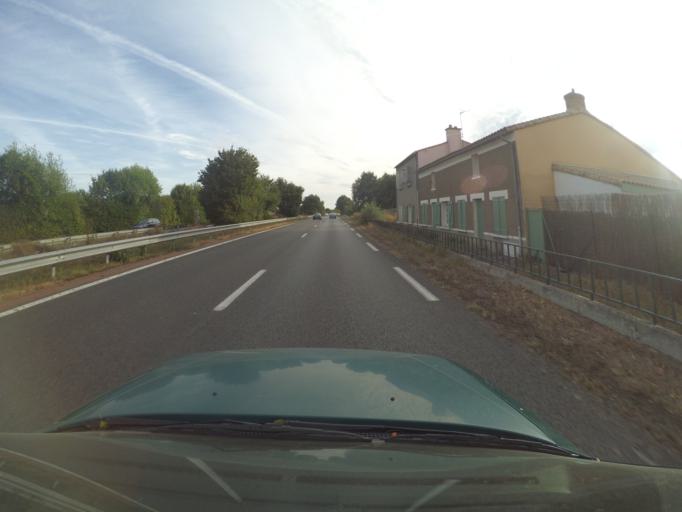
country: FR
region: Pays de la Loire
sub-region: Departement de la Vendee
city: Bouffere
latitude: 46.9268
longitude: -1.3642
